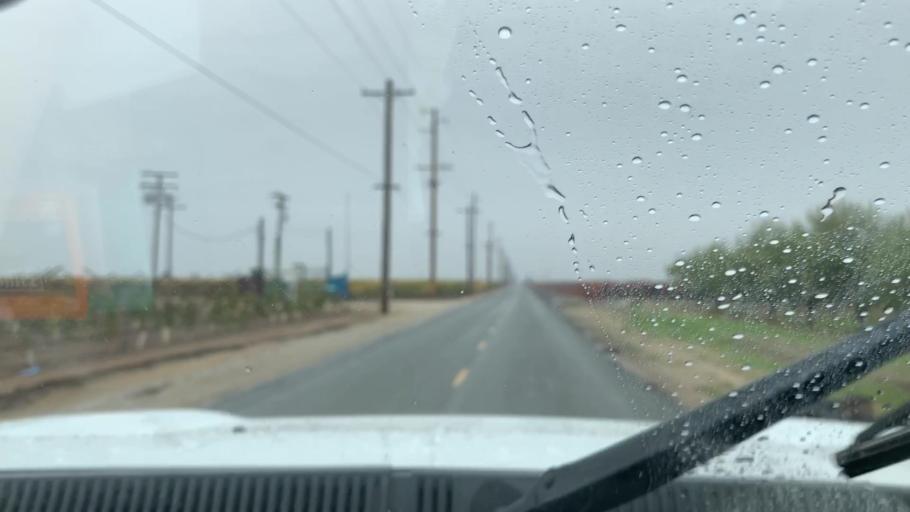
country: US
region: California
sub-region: Tulare County
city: Richgrove
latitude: 35.8341
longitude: -119.1708
